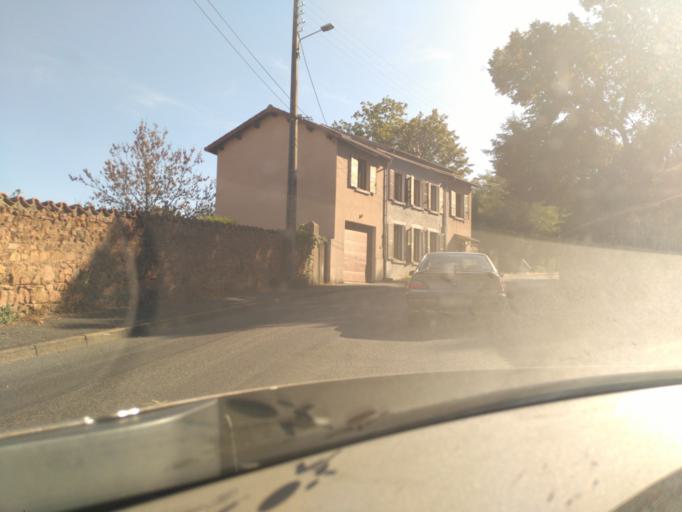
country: FR
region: Rhone-Alpes
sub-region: Departement du Rhone
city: Tarare
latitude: 45.8921
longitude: 4.4345
